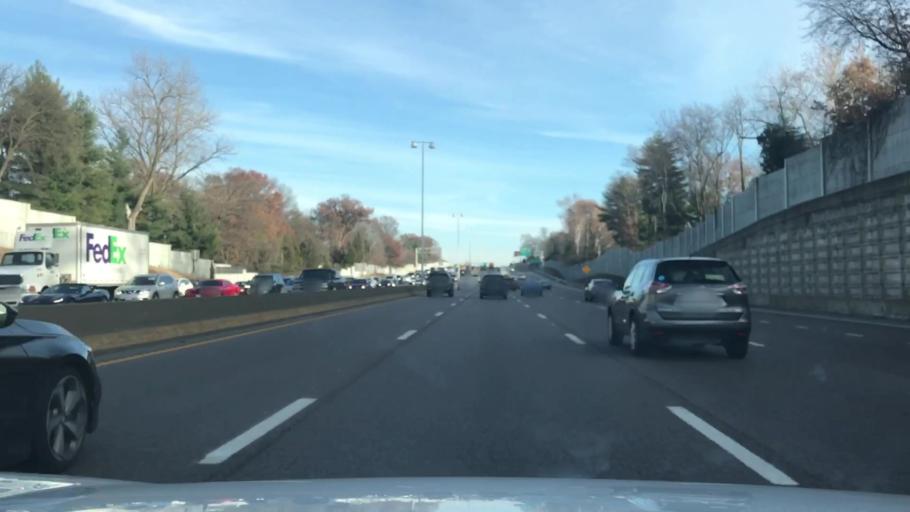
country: US
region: Missouri
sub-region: Saint Louis County
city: Frontenac
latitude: 38.6379
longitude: -90.4355
